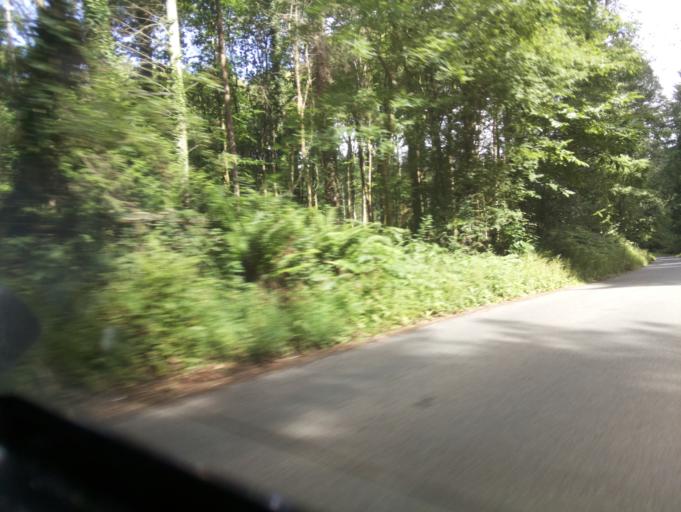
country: GB
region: England
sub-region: Gloucestershire
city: Cinderford
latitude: 51.7975
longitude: -2.4938
